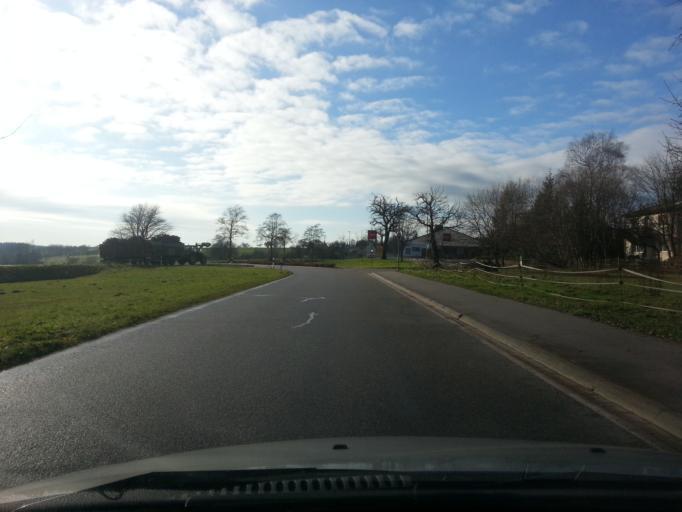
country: DE
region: Baden-Wuerttemberg
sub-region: Karlsruhe Region
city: Zwingenberg
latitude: 49.4645
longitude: 9.0857
